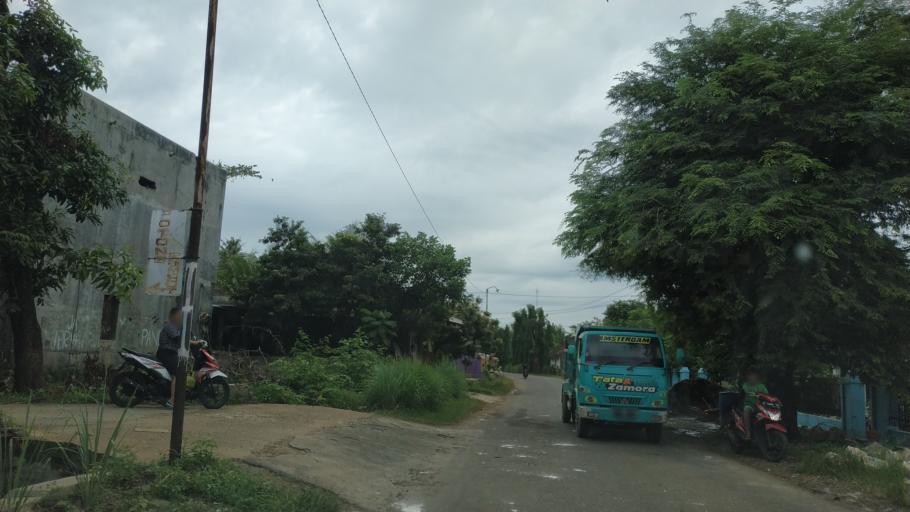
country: ID
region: Central Java
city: Krajan Tegalombo
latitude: -6.4442
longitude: 110.9842
